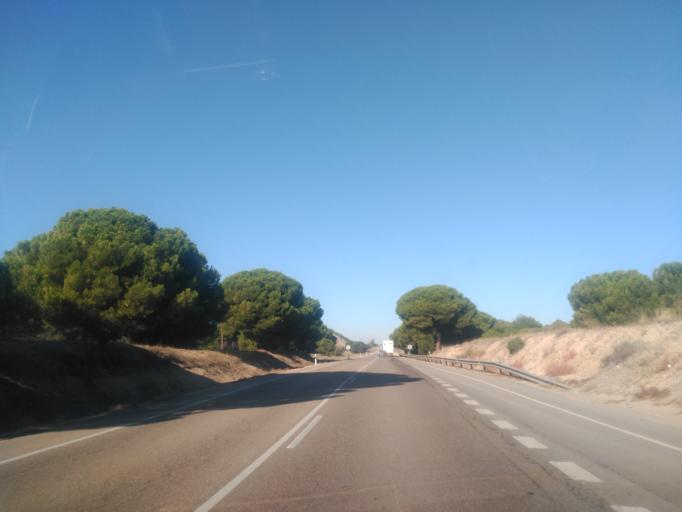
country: ES
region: Castille and Leon
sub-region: Provincia de Valladolid
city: Manzanillo
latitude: 41.6133
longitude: -4.1792
